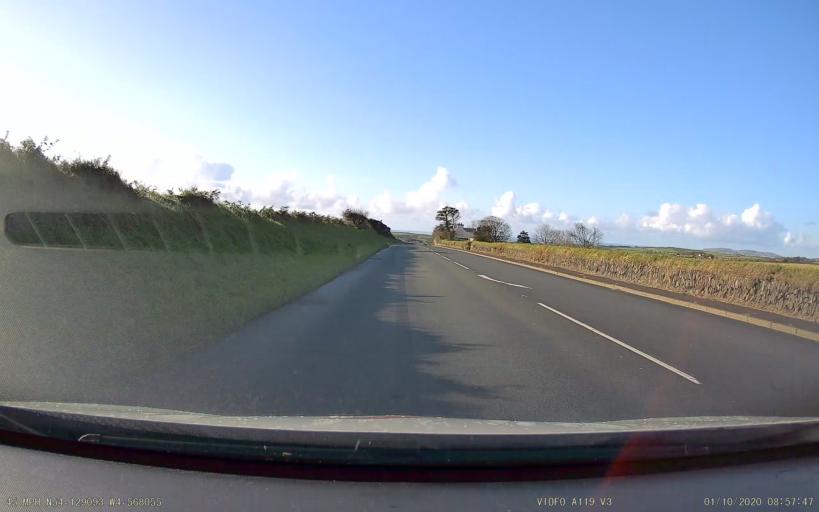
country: IM
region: Douglas
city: Douglas
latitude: 54.1291
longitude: -4.5681
